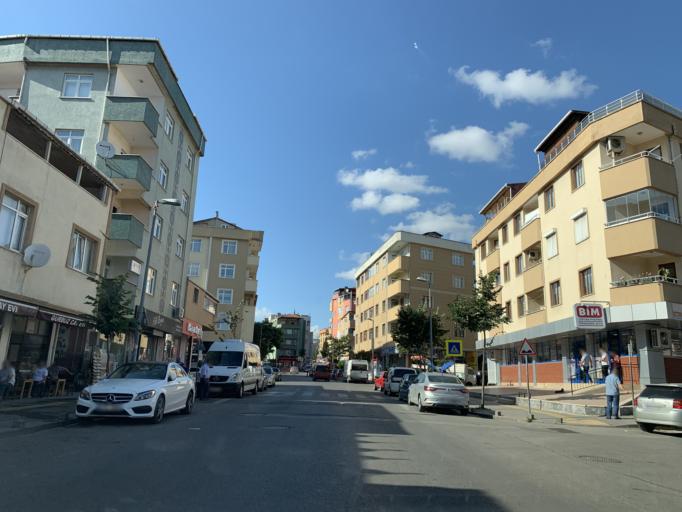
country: TR
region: Istanbul
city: Pendik
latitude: 40.8848
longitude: 29.2726
